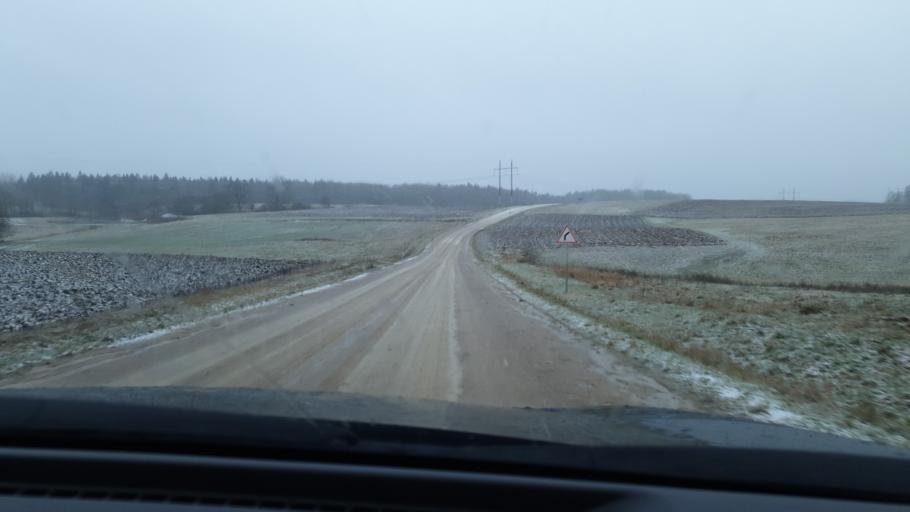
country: LT
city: Jieznas
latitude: 54.5540
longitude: 24.3149
